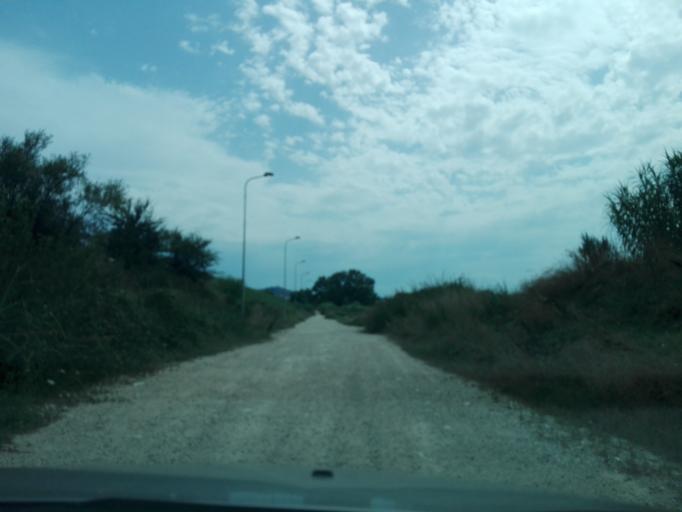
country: IT
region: Abruzzo
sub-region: Provincia di Pescara
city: Cappelle sul Tavo
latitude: 42.4910
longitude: 14.1123
